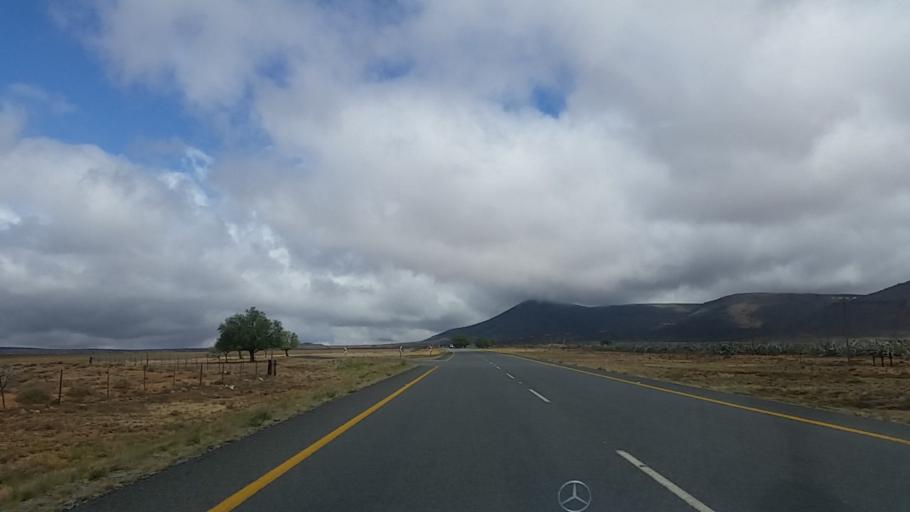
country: ZA
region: Eastern Cape
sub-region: Cacadu District Municipality
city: Graaff-Reinet
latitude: -32.0199
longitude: 24.6397
